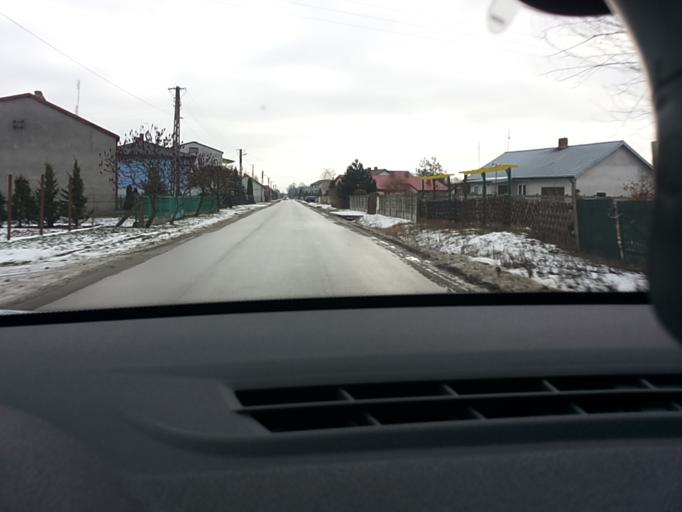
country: PL
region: Lodz Voivodeship
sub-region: Powiat skierniewicki
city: Makow
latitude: 52.0041
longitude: 20.0720
